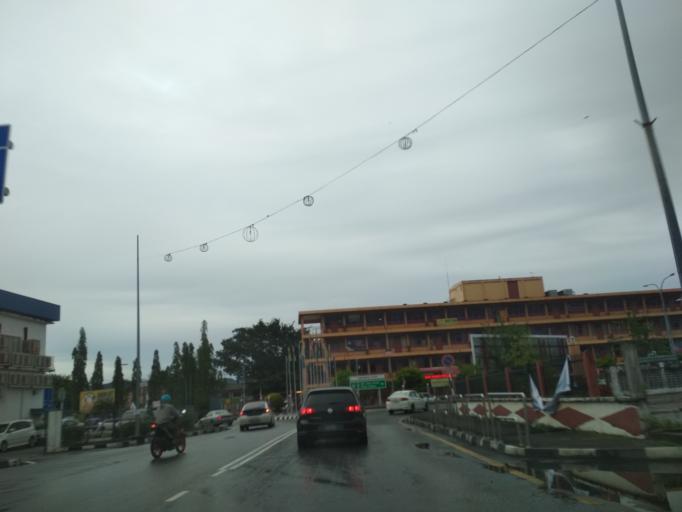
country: MY
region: Perlis
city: Kangar
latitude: 6.4390
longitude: 100.1934
